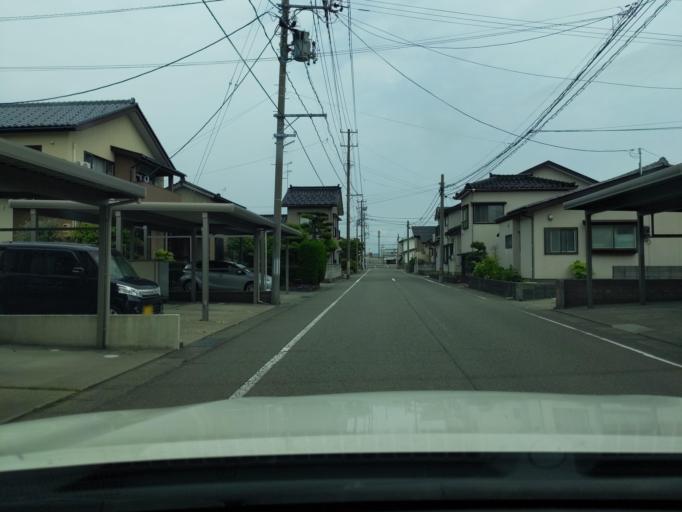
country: JP
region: Niigata
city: Kashiwazaki
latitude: 37.3628
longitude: 138.5598
